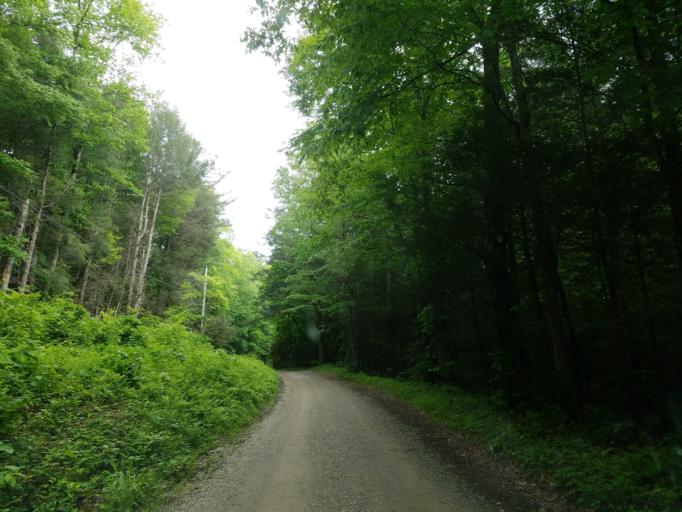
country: US
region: Georgia
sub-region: Union County
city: Blairsville
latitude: 34.7336
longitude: -83.9709
